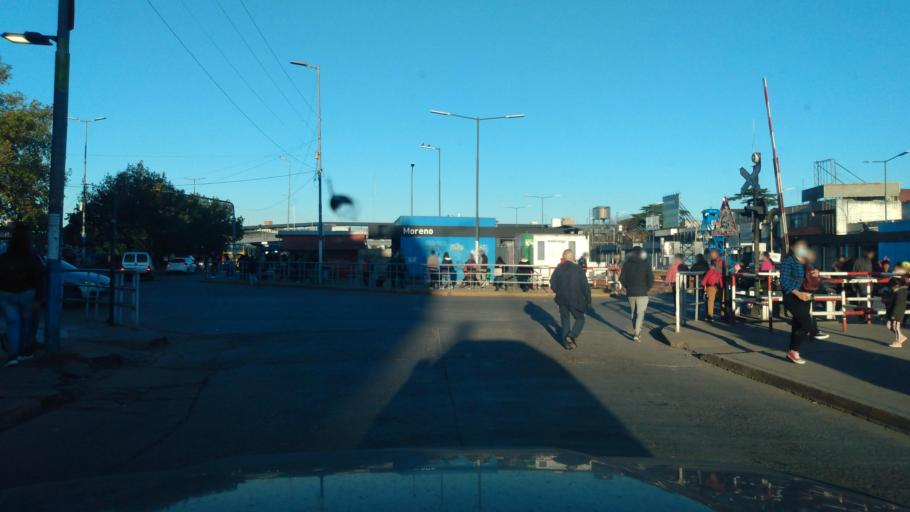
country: AR
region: Buenos Aires
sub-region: Partido de Merlo
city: Merlo
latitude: -34.6497
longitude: -58.7919
